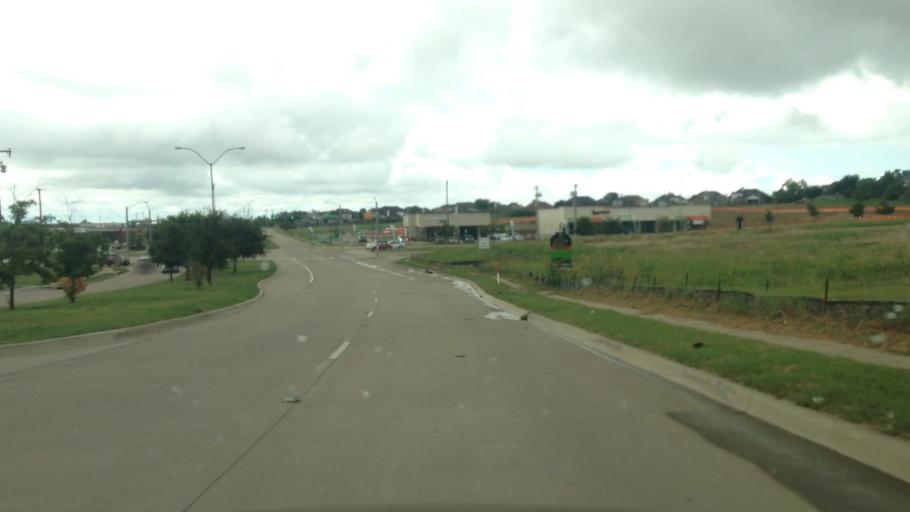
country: US
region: Texas
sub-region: Tarrant County
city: Crowley
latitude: 32.6304
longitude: -97.4068
